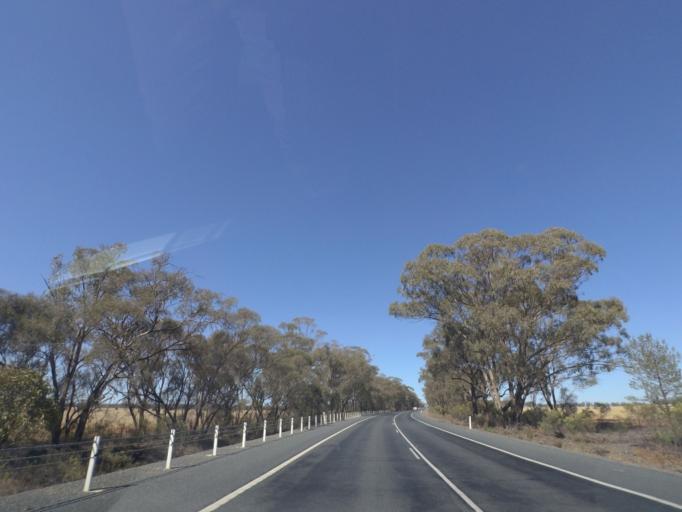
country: AU
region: New South Wales
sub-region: Bland
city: West Wyalong
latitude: -34.1141
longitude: 147.1371
